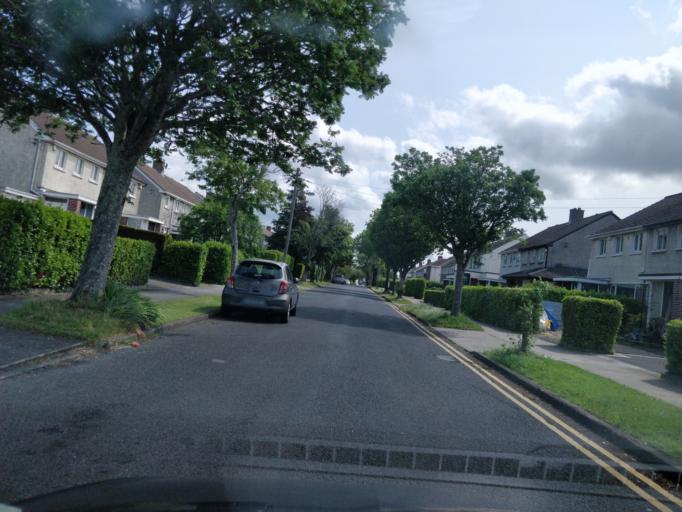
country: IE
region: Leinster
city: Dundrum
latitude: 53.2870
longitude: -6.2516
